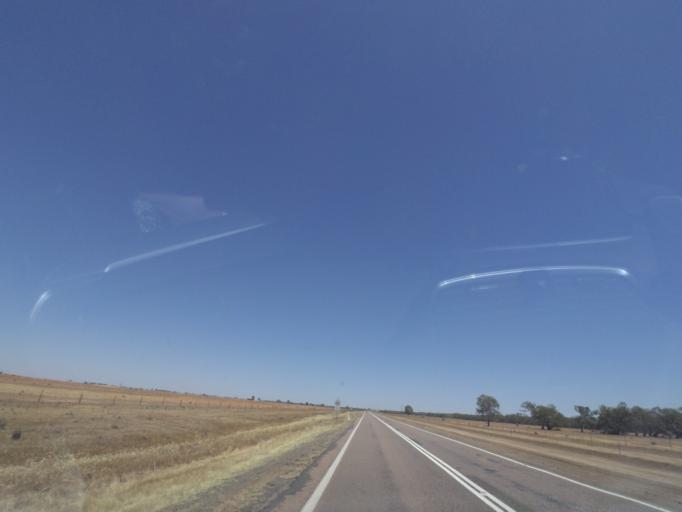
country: AU
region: New South Wales
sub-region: Berrigan
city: Berrigan
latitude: -35.1496
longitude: 146.0007
